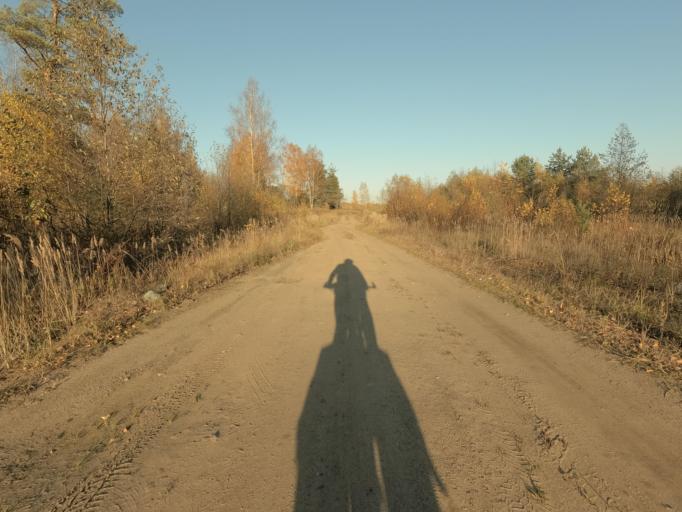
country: RU
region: Leningrad
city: Kirovsk
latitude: 59.8601
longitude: 31.0079
